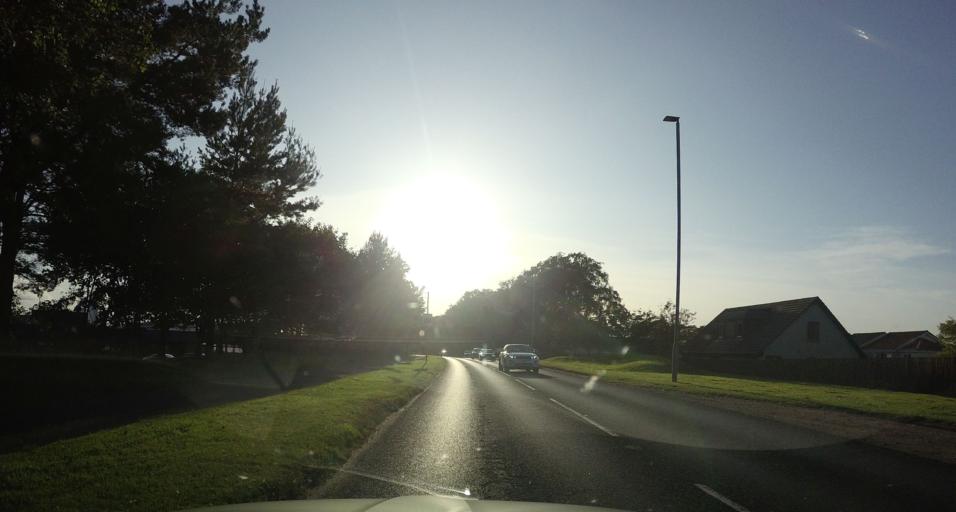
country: GB
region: Scotland
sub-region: Aberdeenshire
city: Westhill
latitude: 57.1500
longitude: -2.2838
